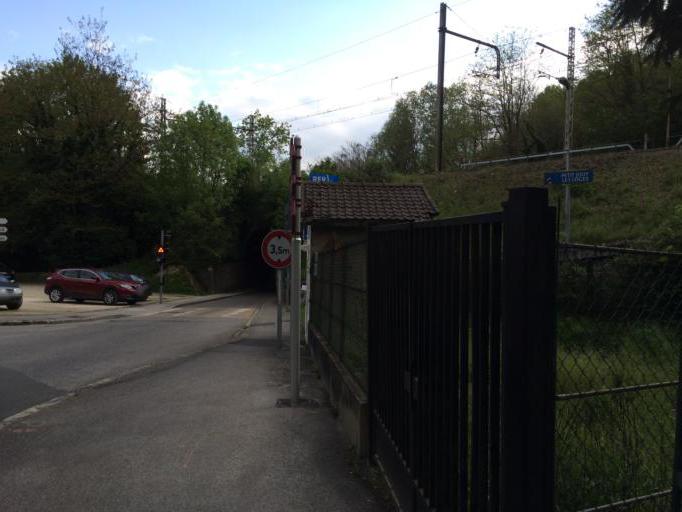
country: FR
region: Ile-de-France
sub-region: Departement des Yvelines
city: Les Loges-en-Josas
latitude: 48.7711
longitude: 2.1473
